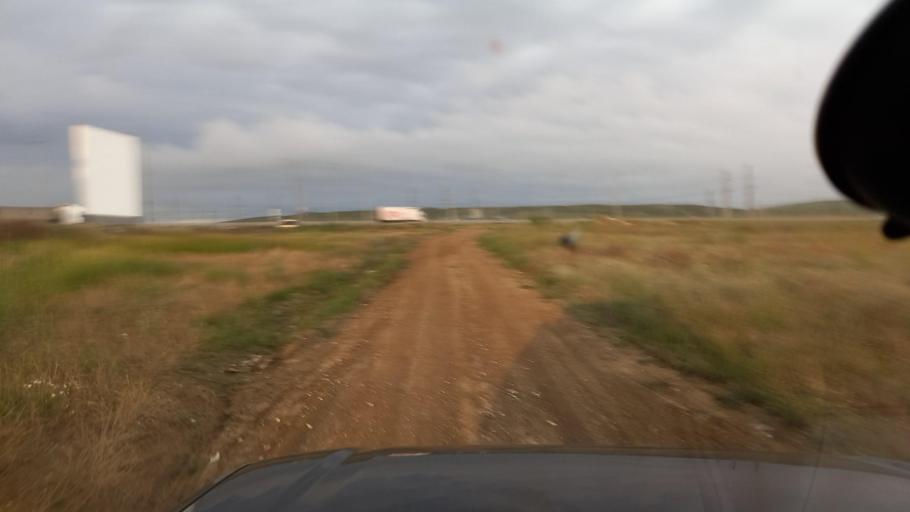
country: RU
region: Krasnodarskiy
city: Taman'
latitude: 45.2094
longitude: 36.7591
